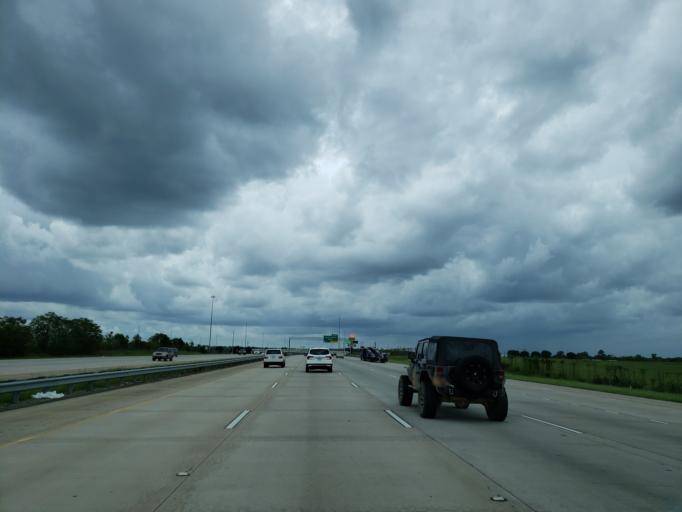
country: US
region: Georgia
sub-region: Peach County
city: Byron
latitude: 32.7221
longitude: -83.7282
